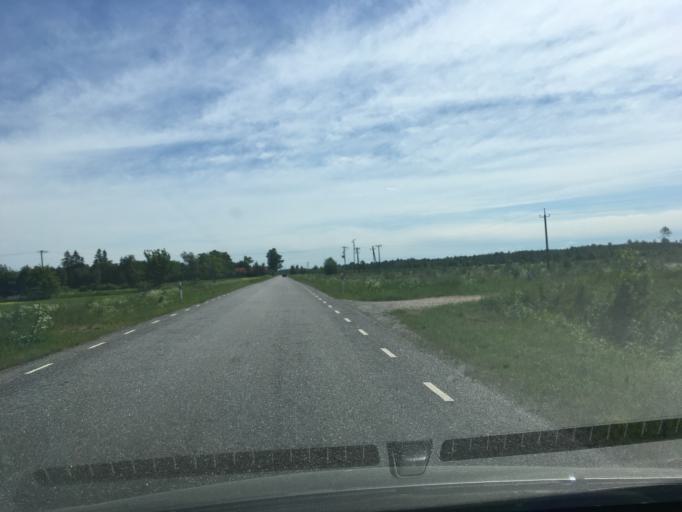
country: EE
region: Paernumaa
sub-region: Audru vald
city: Audru
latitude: 58.4305
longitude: 24.4012
